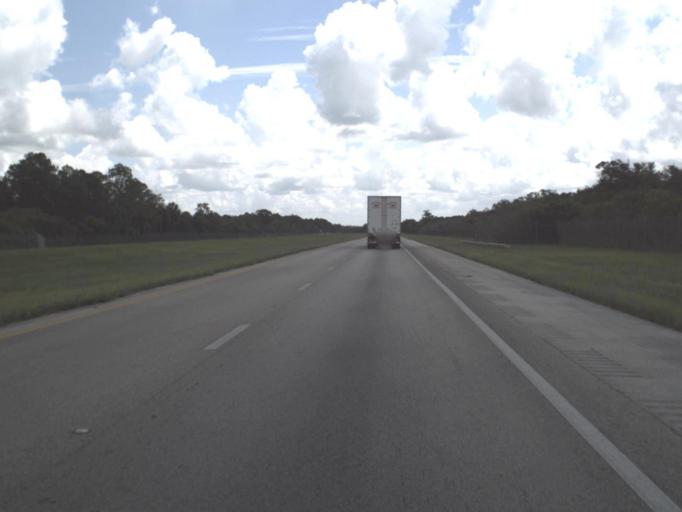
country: US
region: Florida
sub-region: Collier County
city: Orangetree
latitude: 26.1530
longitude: -81.4971
